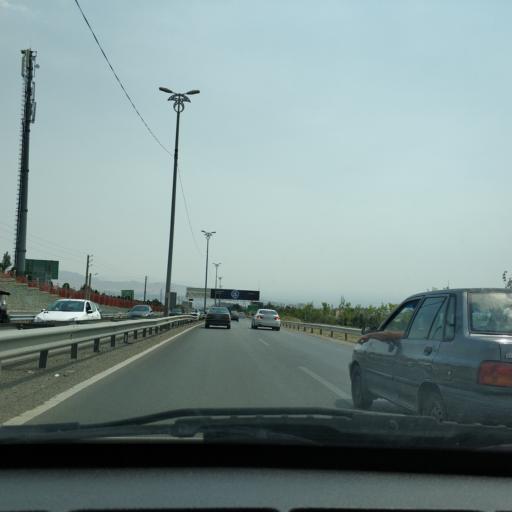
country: IR
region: Tehran
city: Tajrish
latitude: 35.7786
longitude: 51.5619
